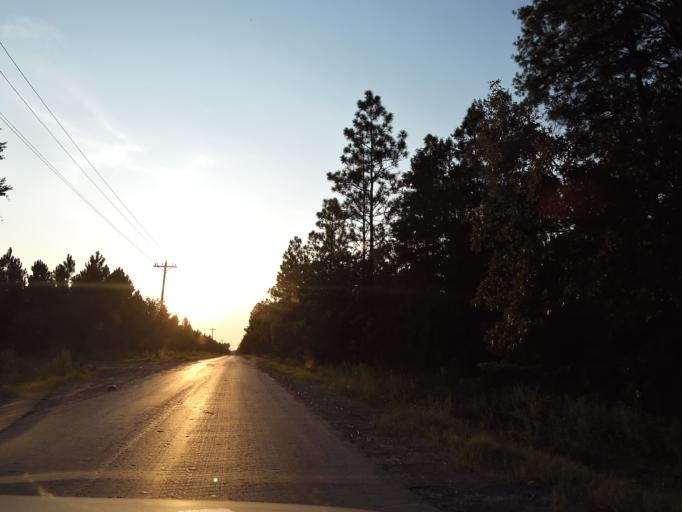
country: US
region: Florida
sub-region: Baker County
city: Macclenny
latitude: 30.3934
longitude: -82.1005
